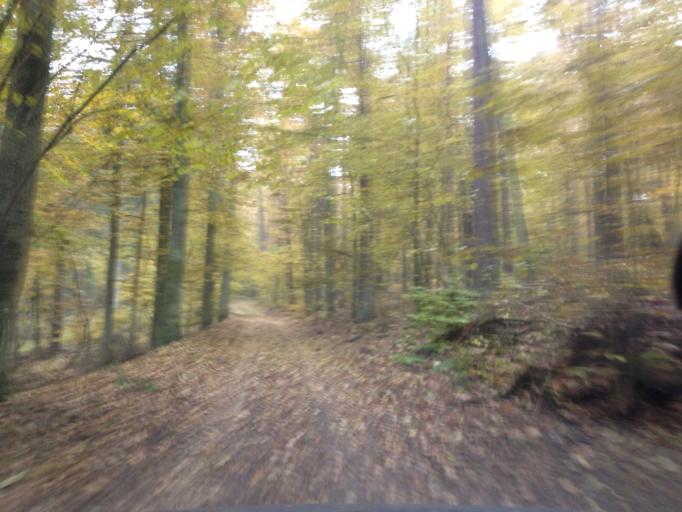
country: PL
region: Kujawsko-Pomorskie
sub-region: Powiat brodnicki
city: Gorzno
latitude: 53.2256
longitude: 19.7150
